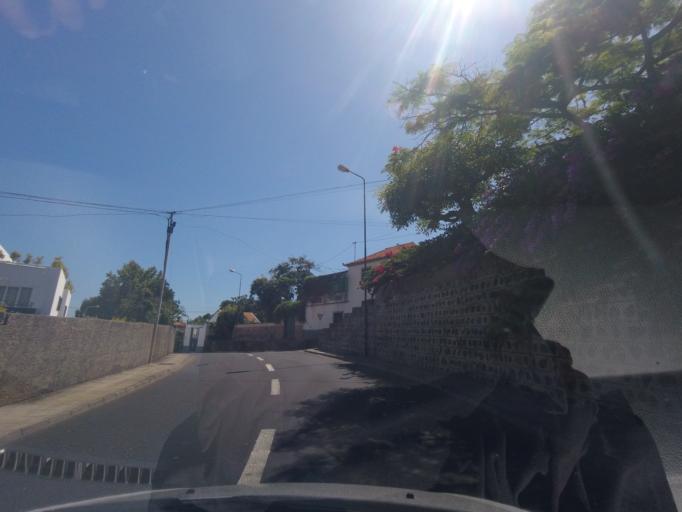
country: PT
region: Madeira
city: Camara de Lobos
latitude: 32.6504
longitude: -16.9352
